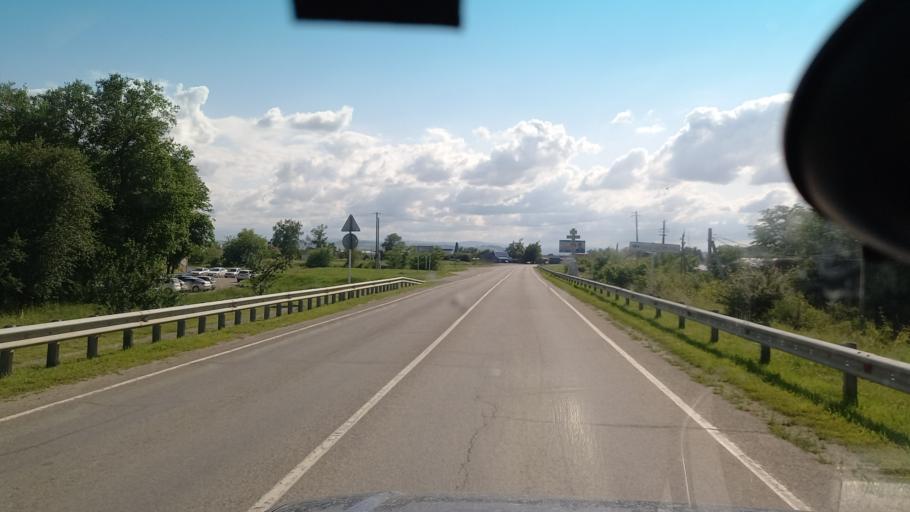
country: RU
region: Krasnodarskiy
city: Mostovskoy
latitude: 44.3991
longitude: 40.8185
